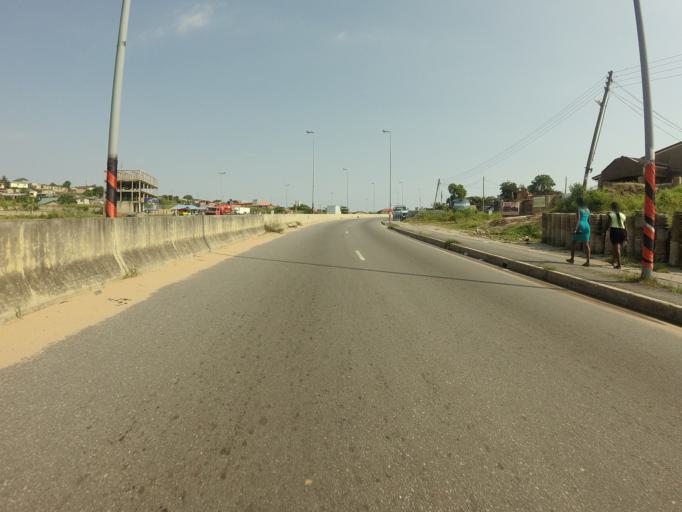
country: GH
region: Greater Accra
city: Gbawe
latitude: 5.6196
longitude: -0.2957
